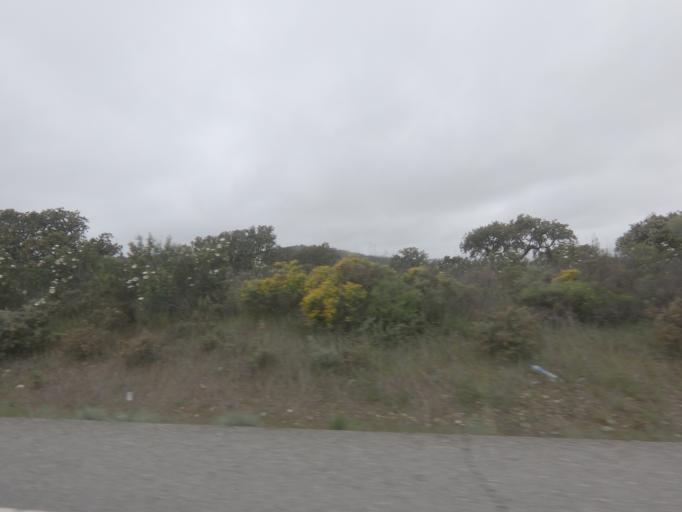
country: ES
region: Extremadura
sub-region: Provincia de Badajoz
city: Puebla de Obando
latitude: 39.2855
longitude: -6.5220
